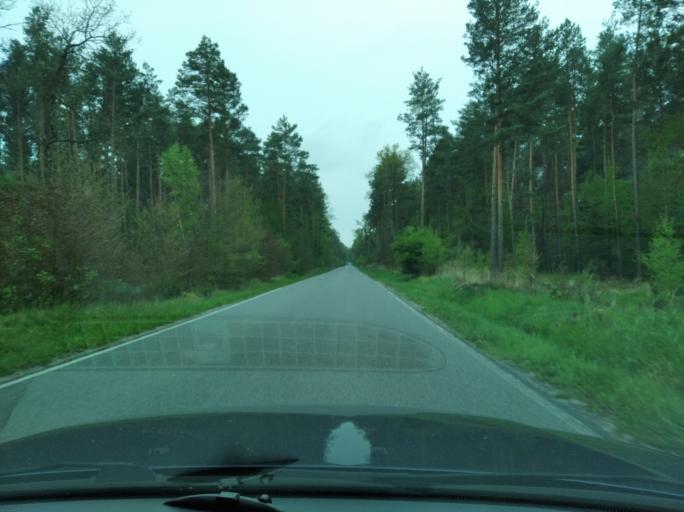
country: PL
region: Subcarpathian Voivodeship
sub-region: Powiat ropczycko-sedziszowski
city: Sedziszow Malopolski
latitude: 50.1448
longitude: 21.7569
